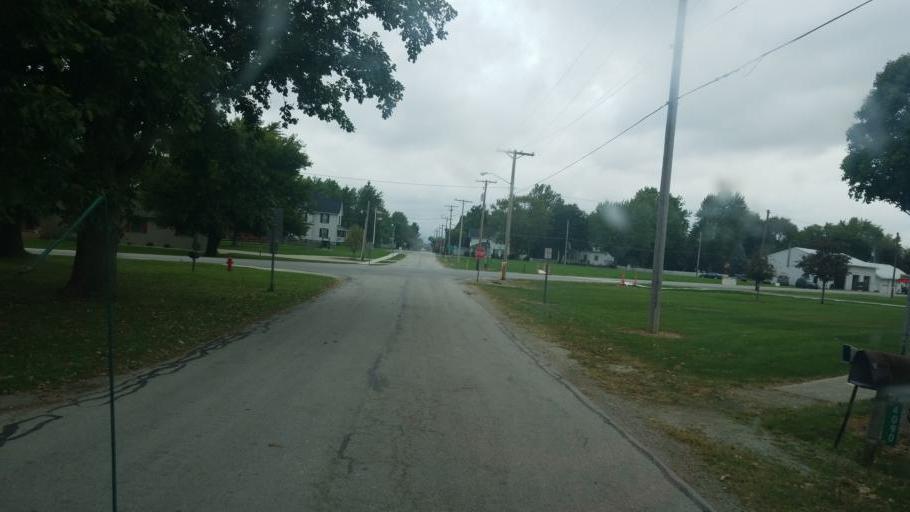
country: US
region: Ohio
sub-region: Seneca County
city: Fostoria
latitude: 41.1069
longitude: -83.5164
